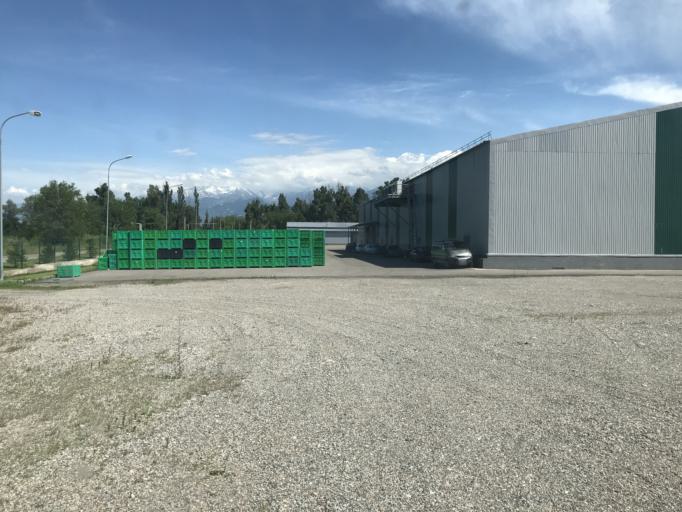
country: KZ
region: Almaty Oblysy
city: Energeticheskiy
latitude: 43.3649
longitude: 77.0797
